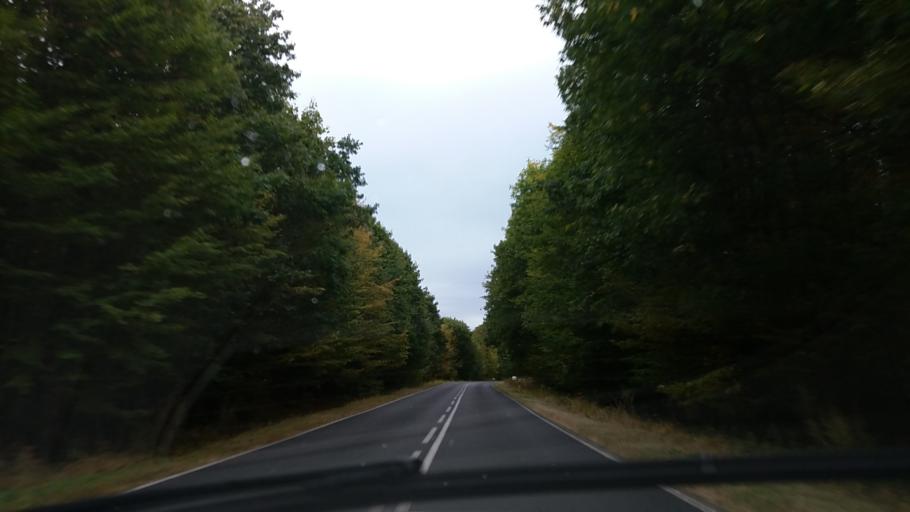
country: PL
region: West Pomeranian Voivodeship
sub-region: Powiat mysliborski
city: Barlinek
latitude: 52.9009
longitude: 15.1927
